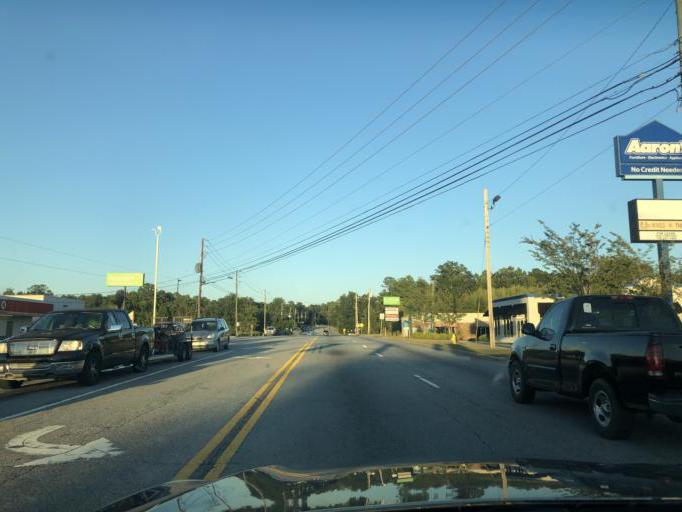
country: US
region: Georgia
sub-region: Muscogee County
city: Columbus
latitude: 32.4676
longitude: -84.9112
